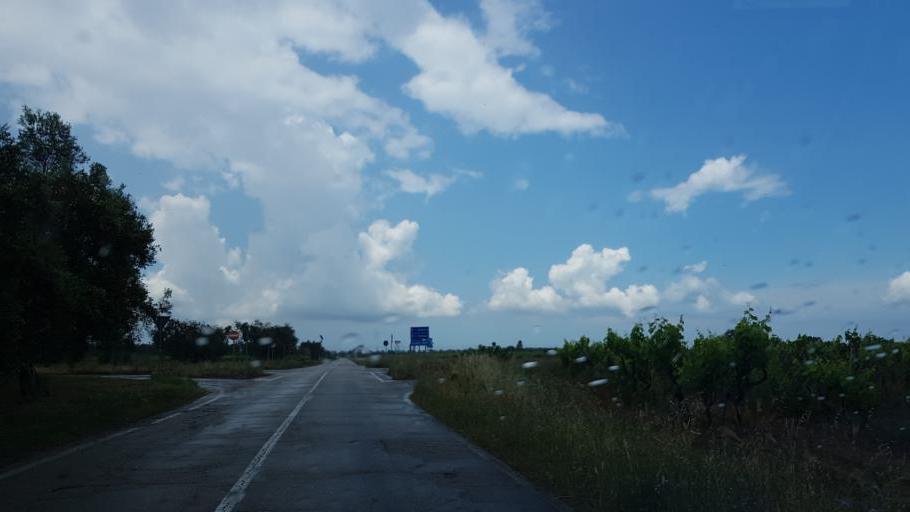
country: IT
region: Apulia
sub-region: Provincia di Brindisi
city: Cellino San Marco
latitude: 40.4809
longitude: 17.9409
